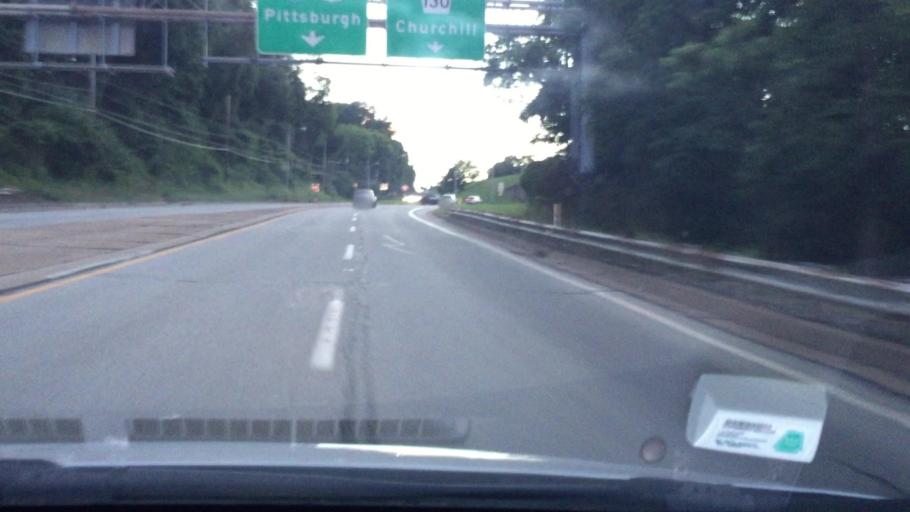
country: US
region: Pennsylvania
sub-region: Allegheny County
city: Churchill
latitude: 40.4389
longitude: -79.8318
